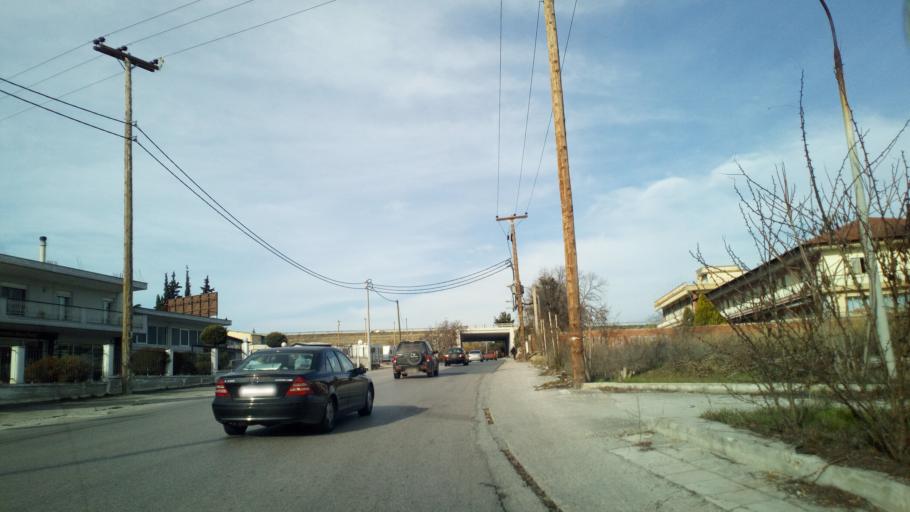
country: GR
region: Central Macedonia
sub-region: Nomos Thessalonikis
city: Lagyna
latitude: 40.7303
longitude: 22.9969
